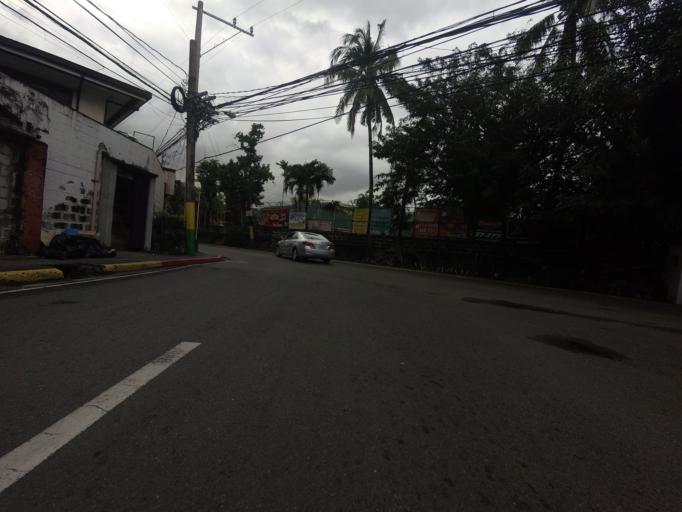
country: PH
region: Metro Manila
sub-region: Mandaluyong
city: Mandaluyong City
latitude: 14.5907
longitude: 121.0427
